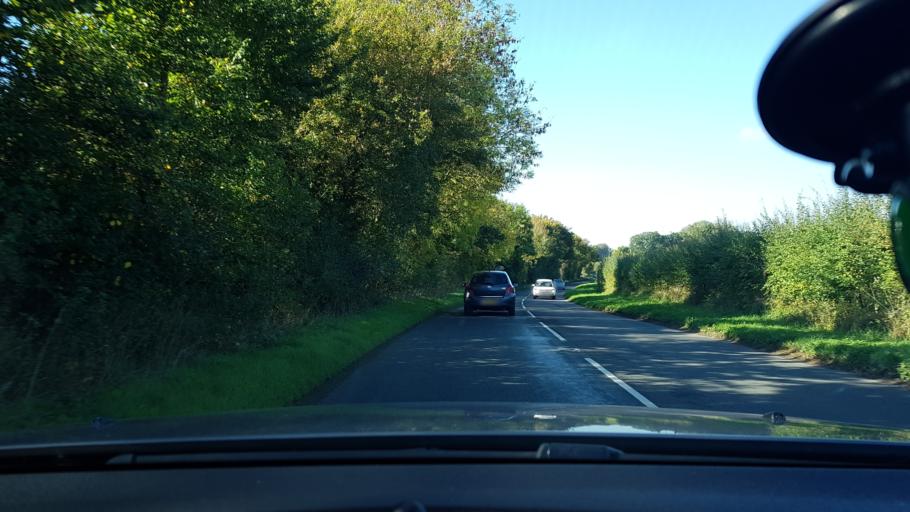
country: GB
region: England
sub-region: Wiltshire
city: Chilton Foliat
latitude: 51.4345
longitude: -1.5552
